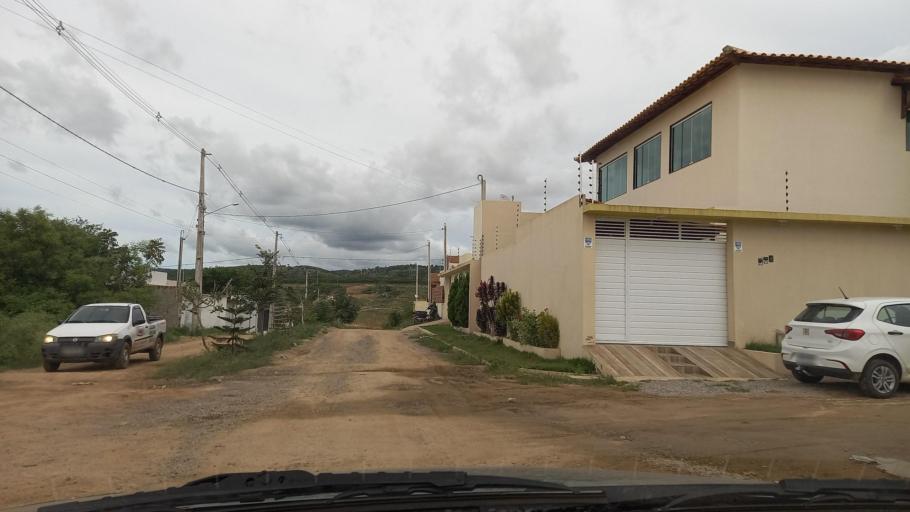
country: BR
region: Pernambuco
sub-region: Gravata
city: Gravata
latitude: -8.2233
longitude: -35.5744
